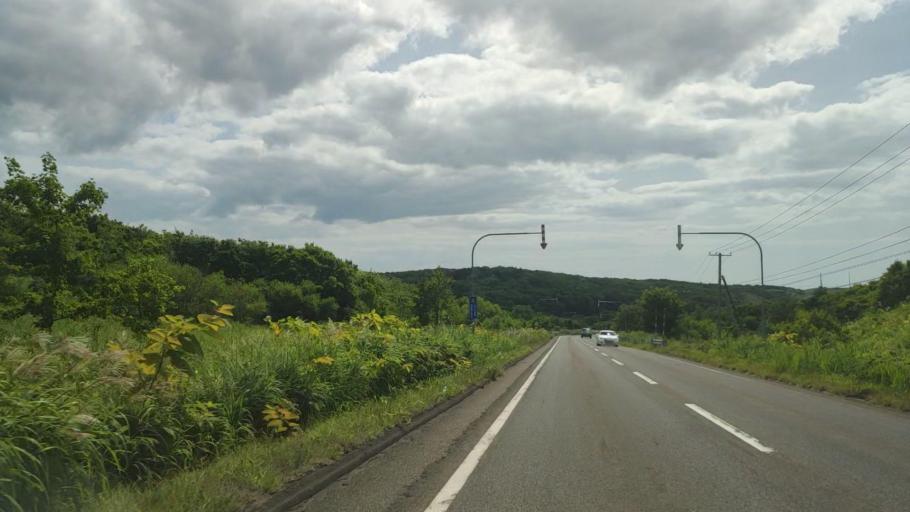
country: JP
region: Hokkaido
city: Rumoi
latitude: 44.6096
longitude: 141.7991
